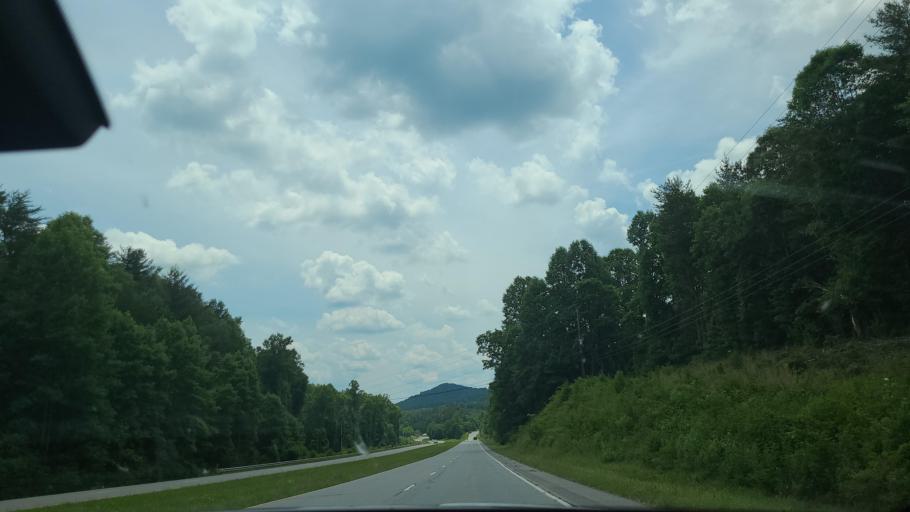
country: US
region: Georgia
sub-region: Fannin County
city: McCaysville
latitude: 35.0174
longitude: -84.2563
